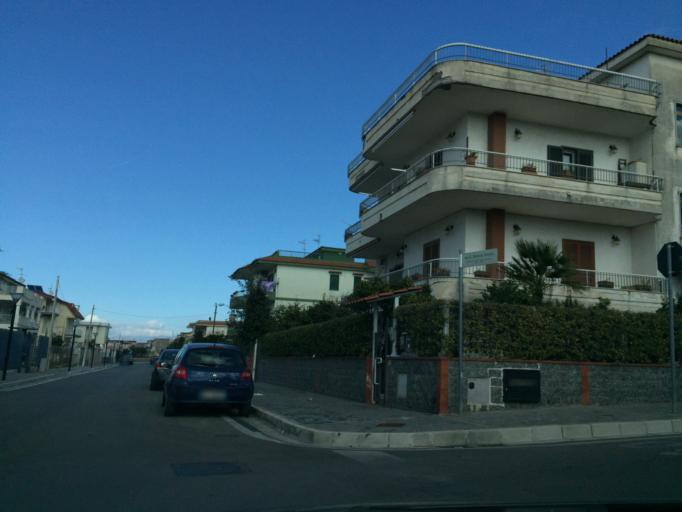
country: IT
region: Campania
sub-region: Provincia di Napoli
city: Pollena Trocchia
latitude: 40.8518
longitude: 14.3793
